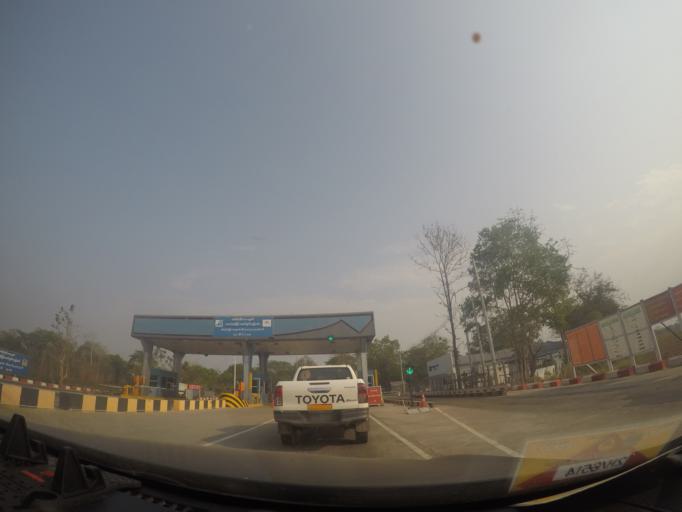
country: MM
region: Bago
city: Paungde
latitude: 18.3576
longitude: 95.6095
